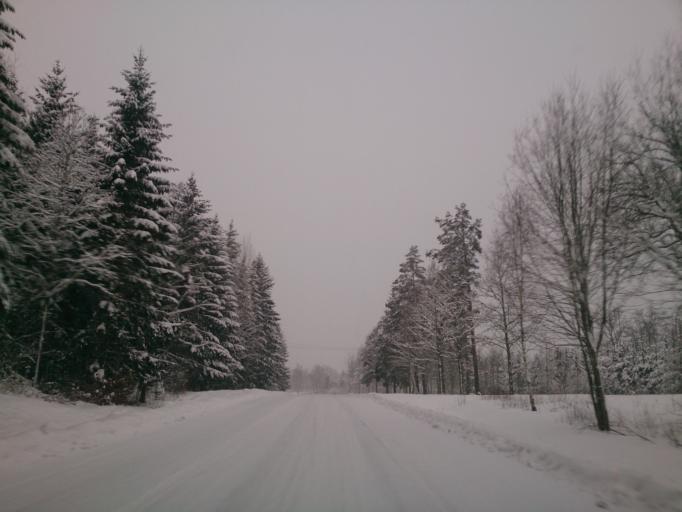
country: SE
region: OEstergoetland
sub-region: Atvidabergs Kommun
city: Atvidaberg
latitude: 58.3596
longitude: 16.0307
